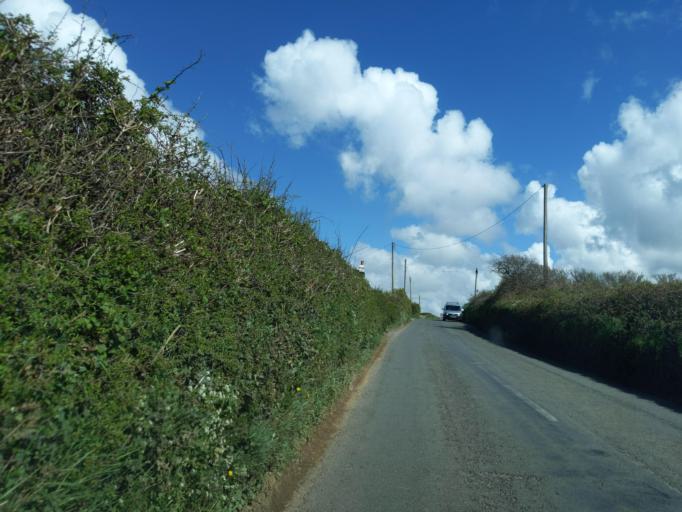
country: GB
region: England
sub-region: Cornwall
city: Wadebridge
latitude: 50.5734
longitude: -4.8354
